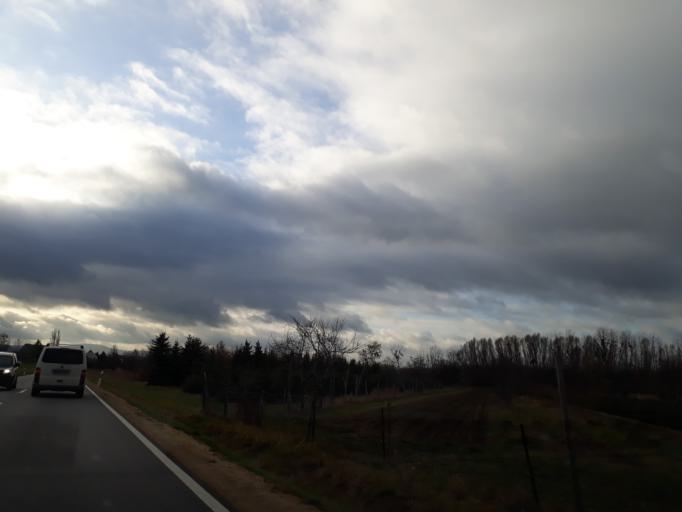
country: DE
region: Saxony
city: Weissenberg
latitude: 51.1909
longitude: 14.6468
